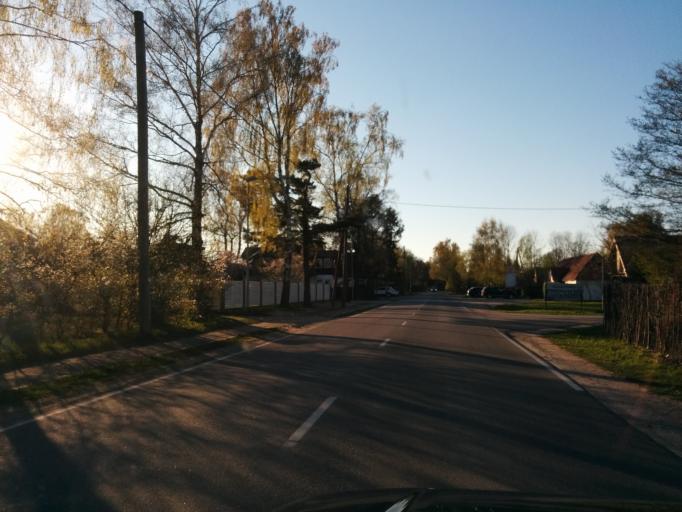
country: LV
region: Engure
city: Smarde
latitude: 57.0259
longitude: 23.4894
